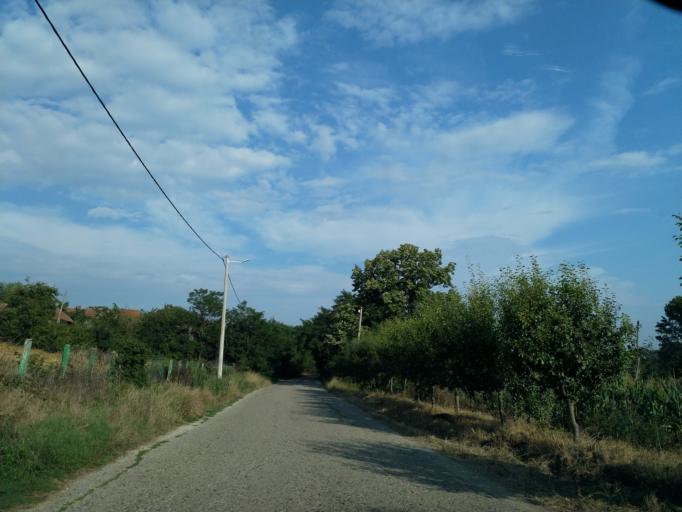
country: RS
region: Central Serbia
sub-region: Pomoravski Okrug
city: Jagodina
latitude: 44.0060
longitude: 21.1798
